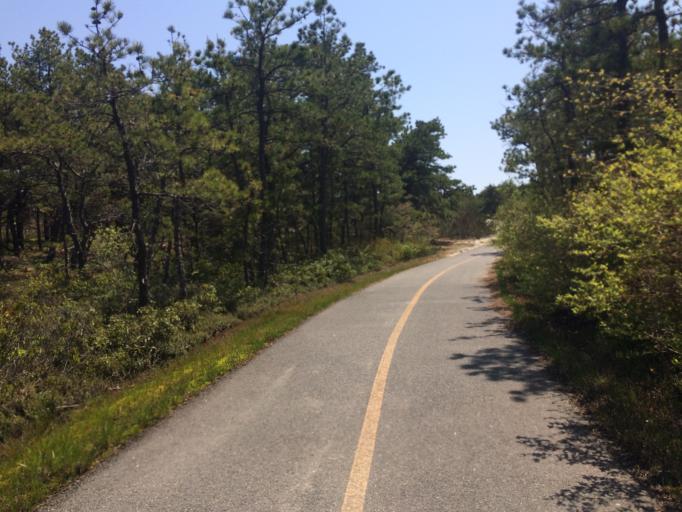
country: US
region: Massachusetts
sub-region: Barnstable County
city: Provincetown
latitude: 42.0617
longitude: -70.2167
